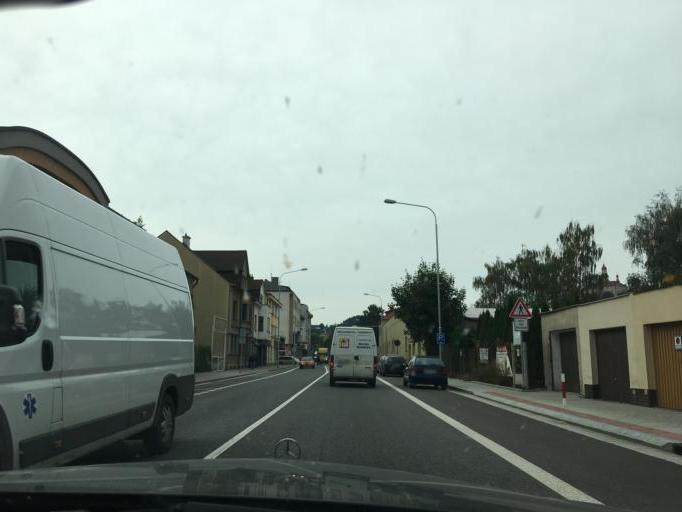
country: CZ
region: Kralovehradecky
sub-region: Okres Nachod
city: Nachod
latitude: 50.4169
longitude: 16.1728
